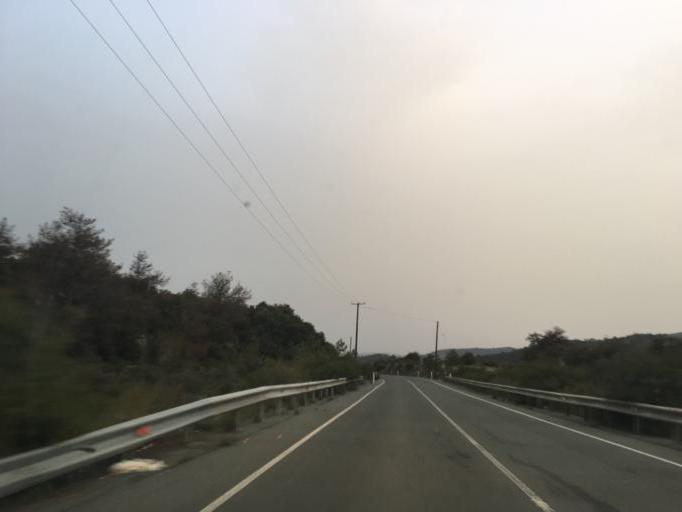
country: CY
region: Limassol
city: Parekklisha
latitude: 34.8056
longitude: 33.1447
